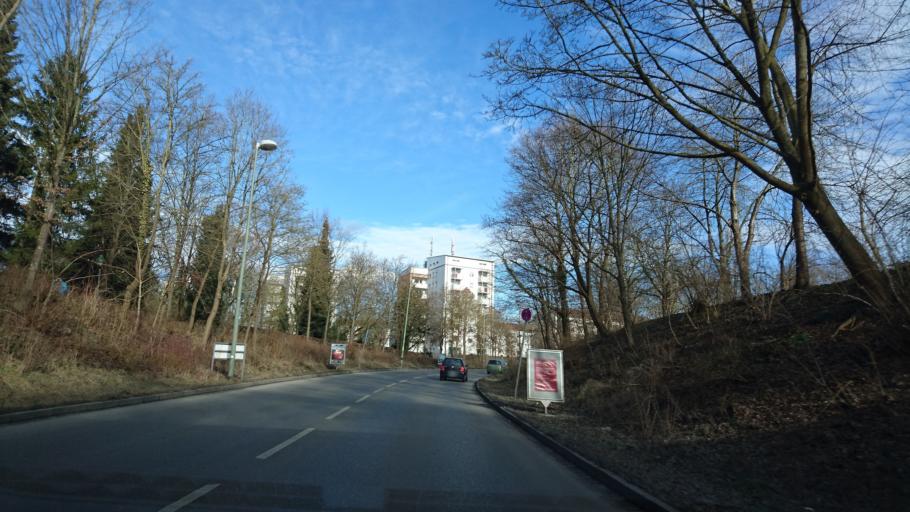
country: DE
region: Bavaria
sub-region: Swabia
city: Augsburg
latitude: 48.3881
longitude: 10.8757
